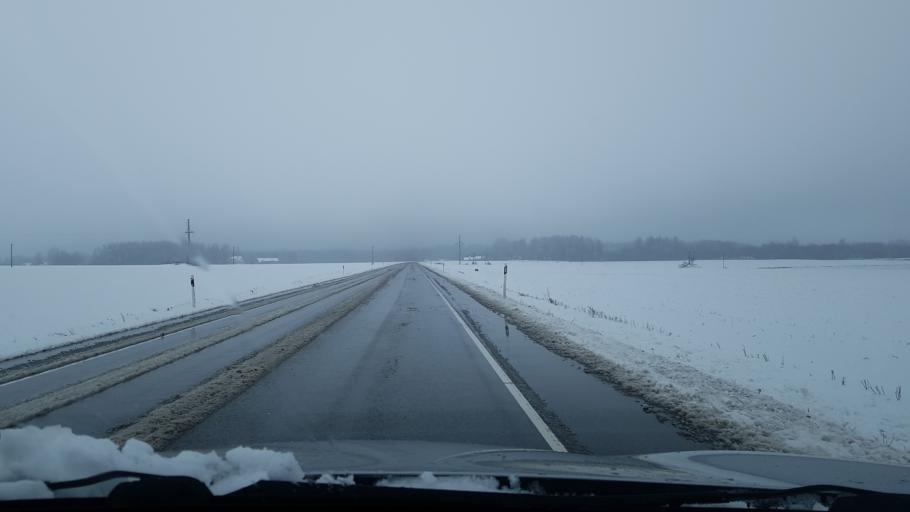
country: EE
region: Vorumaa
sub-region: Voru linn
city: Voru
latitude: 57.8618
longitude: 27.0968
